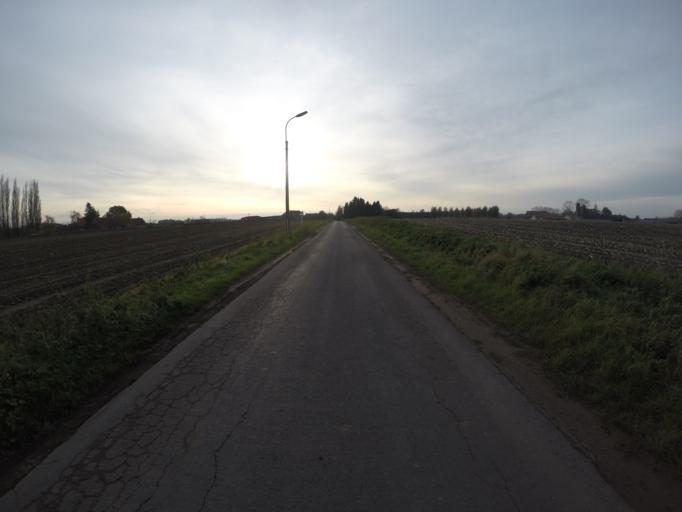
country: BE
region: Flanders
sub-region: Provincie Oost-Vlaanderen
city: Aalter
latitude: 51.0593
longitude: 3.4834
